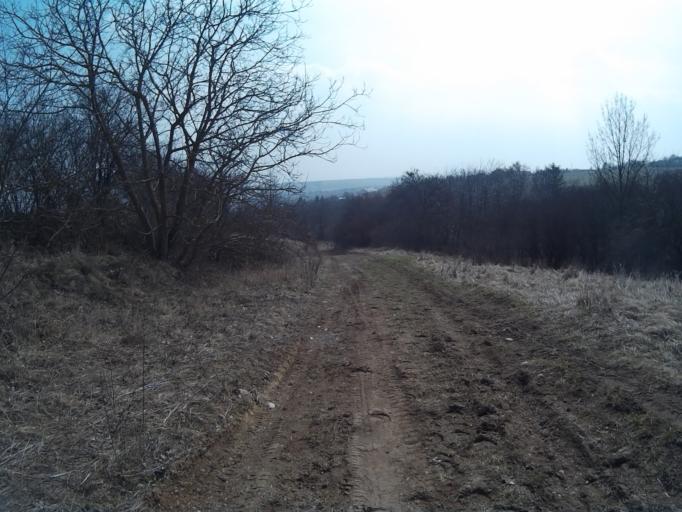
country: CZ
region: South Moravian
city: Pozorice
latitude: 49.2156
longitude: 16.8061
